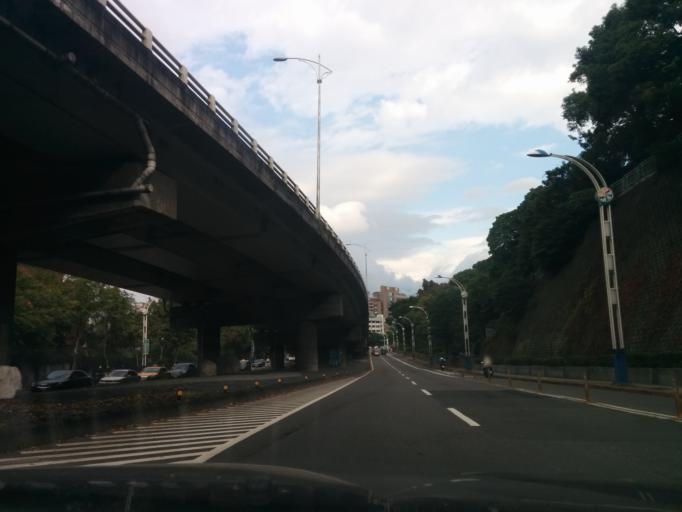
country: TW
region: Taipei
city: Taipei
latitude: 25.0772
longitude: 121.5252
